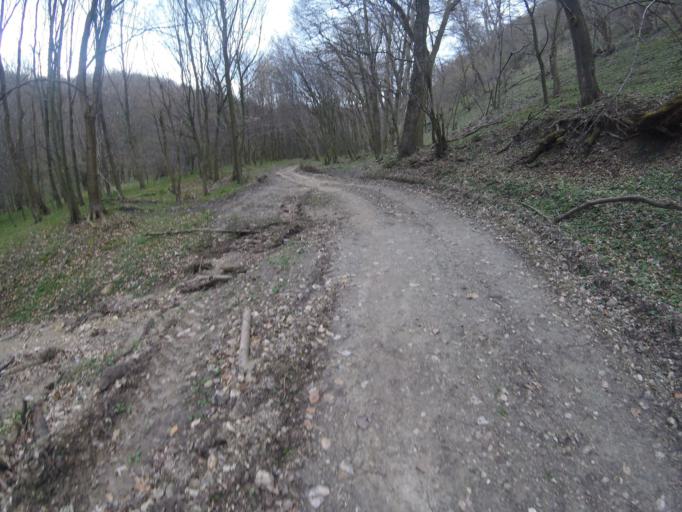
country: HU
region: Fejer
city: Szarliget
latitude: 47.4663
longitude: 18.4469
